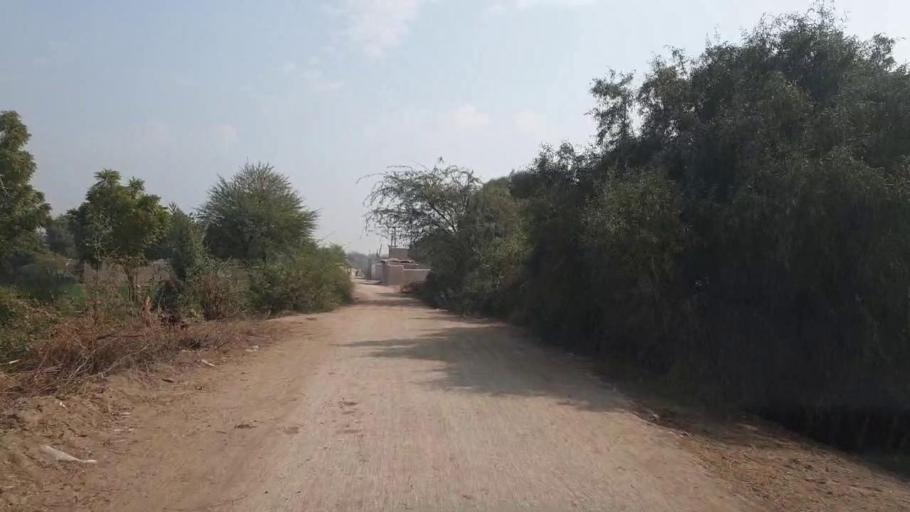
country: PK
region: Sindh
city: Hala
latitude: 25.7951
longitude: 68.4397
